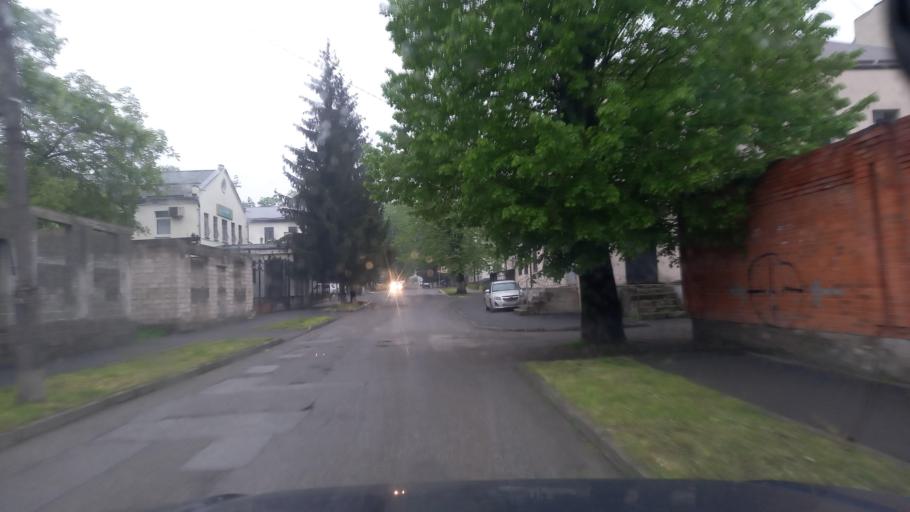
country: RU
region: North Ossetia
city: Alagir
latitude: 43.0403
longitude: 44.2220
